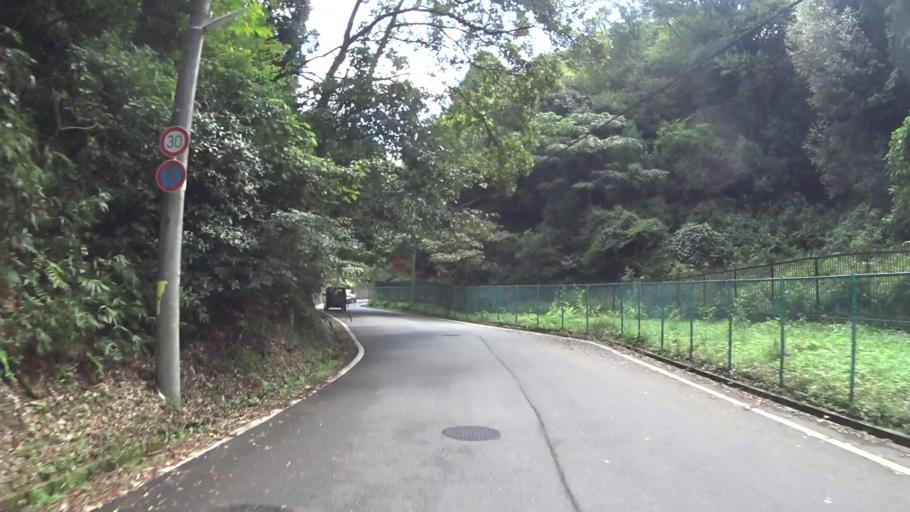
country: JP
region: Kyoto
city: Kyoto
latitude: 34.9808
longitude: 135.7855
